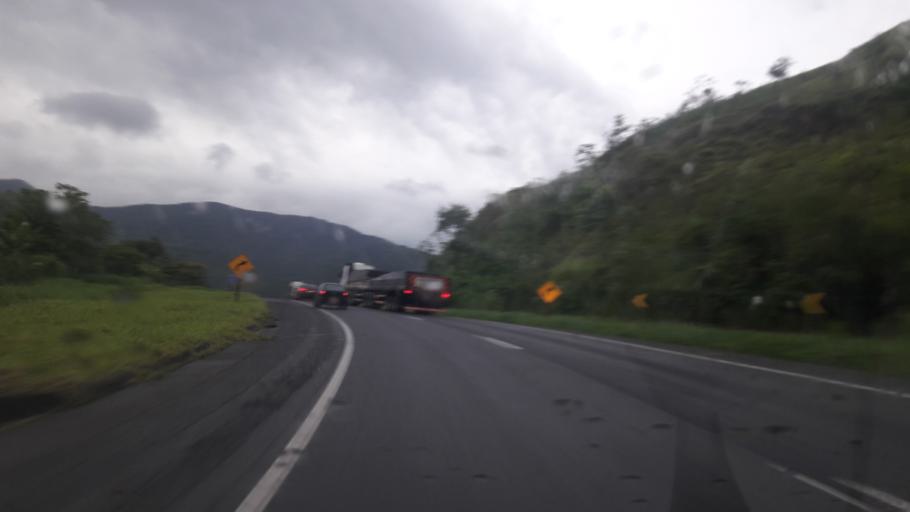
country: BR
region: Sao Paulo
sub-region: Cajati
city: Cajati
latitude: -24.8432
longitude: -48.2108
